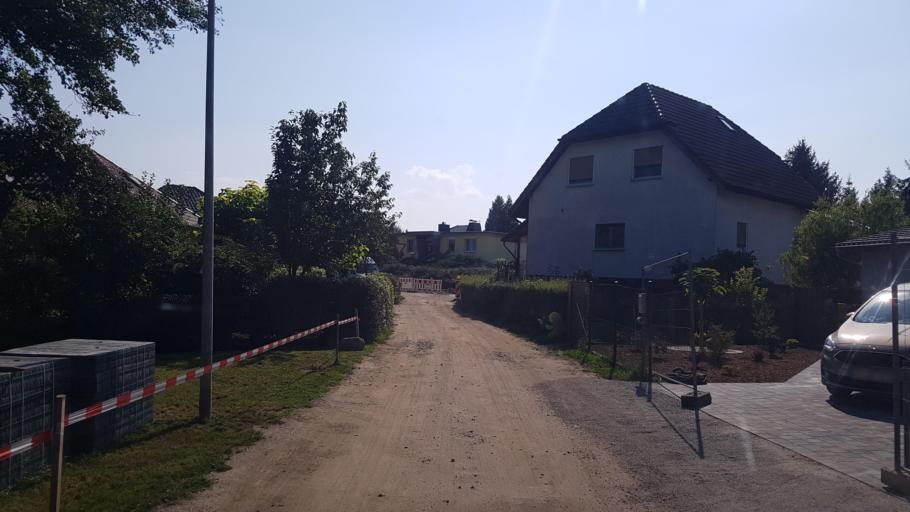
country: DE
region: Brandenburg
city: Vetschau
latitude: 51.7918
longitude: 14.0691
